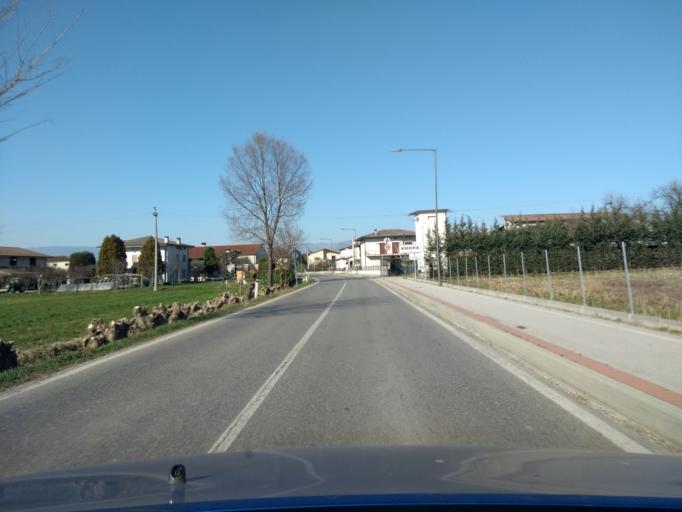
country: IT
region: Veneto
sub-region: Provincia di Vicenza
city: Pozzoleone
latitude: 45.6285
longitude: 11.6595
